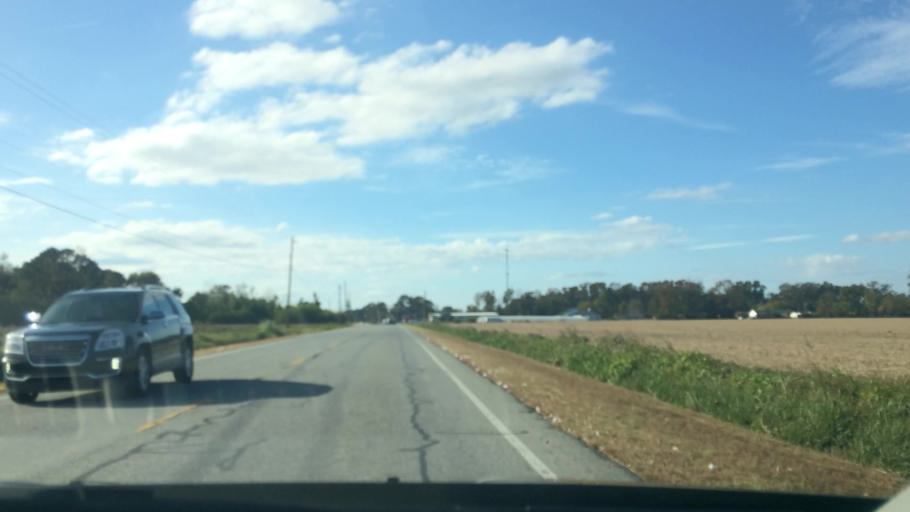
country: US
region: North Carolina
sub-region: Greene County
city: Snow Hill
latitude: 35.4393
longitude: -77.7857
